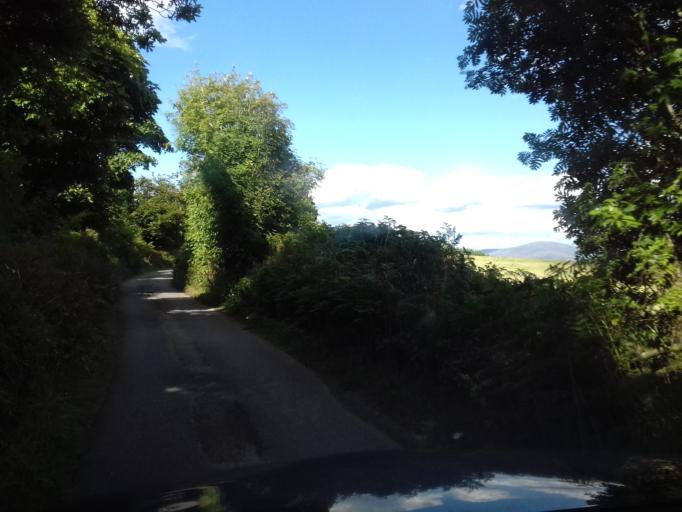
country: IE
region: Leinster
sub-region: Kilkenny
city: Graiguenamanagh
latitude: 52.5614
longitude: -7.0096
